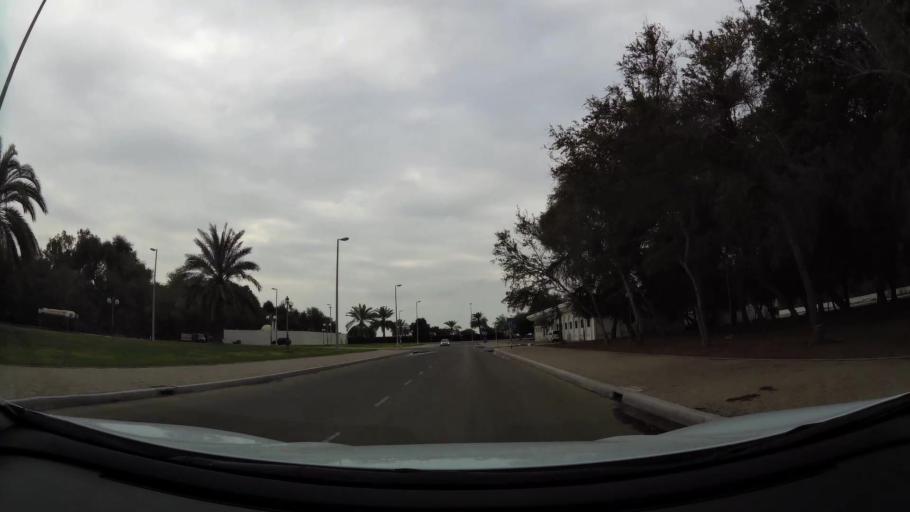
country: AE
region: Abu Dhabi
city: Abu Dhabi
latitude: 24.4290
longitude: 54.3797
